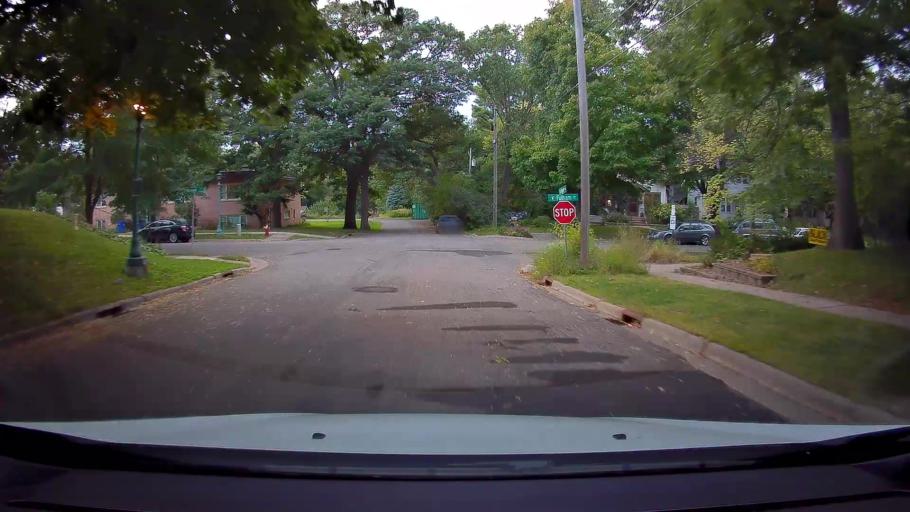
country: US
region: Minnesota
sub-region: Ramsey County
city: Lauderdale
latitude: 44.9881
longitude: -93.1969
